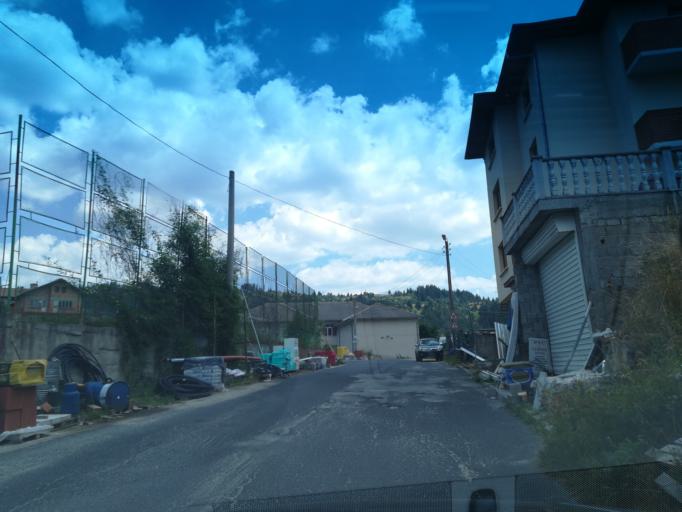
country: BG
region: Smolyan
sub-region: Obshtina Smolyan
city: Smolyan
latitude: 41.6604
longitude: 24.7718
